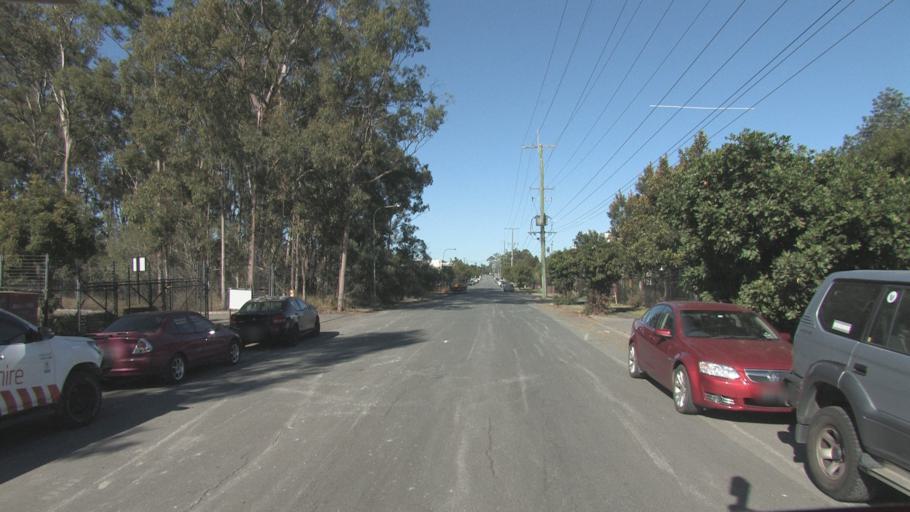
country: AU
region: Queensland
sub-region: Logan
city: Slacks Creek
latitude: -27.6597
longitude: 153.1338
